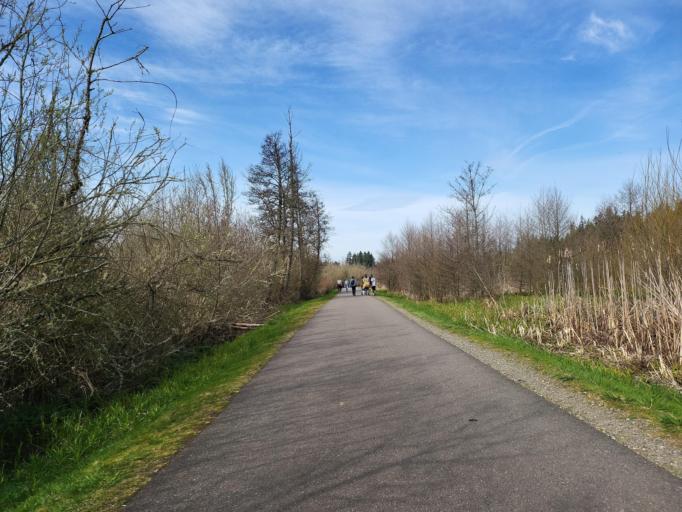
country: US
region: Washington
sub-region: King County
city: East Hill-Meridian
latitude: 47.4057
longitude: -122.1584
